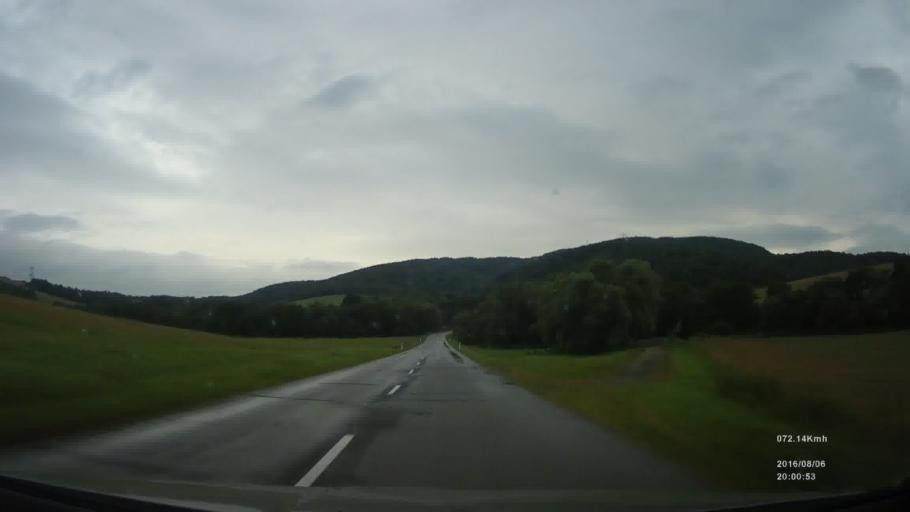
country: SK
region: Presovsky
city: Svidnik
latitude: 49.2480
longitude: 21.5837
